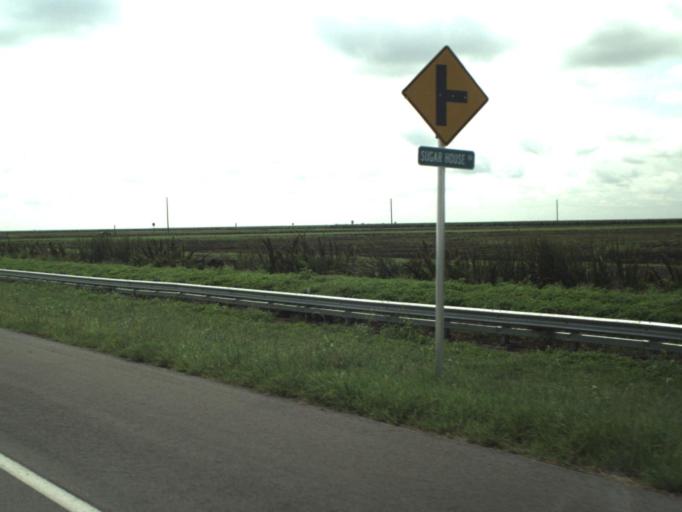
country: US
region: Florida
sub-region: Palm Beach County
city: Belle Glade
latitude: 26.7261
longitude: -80.6540
